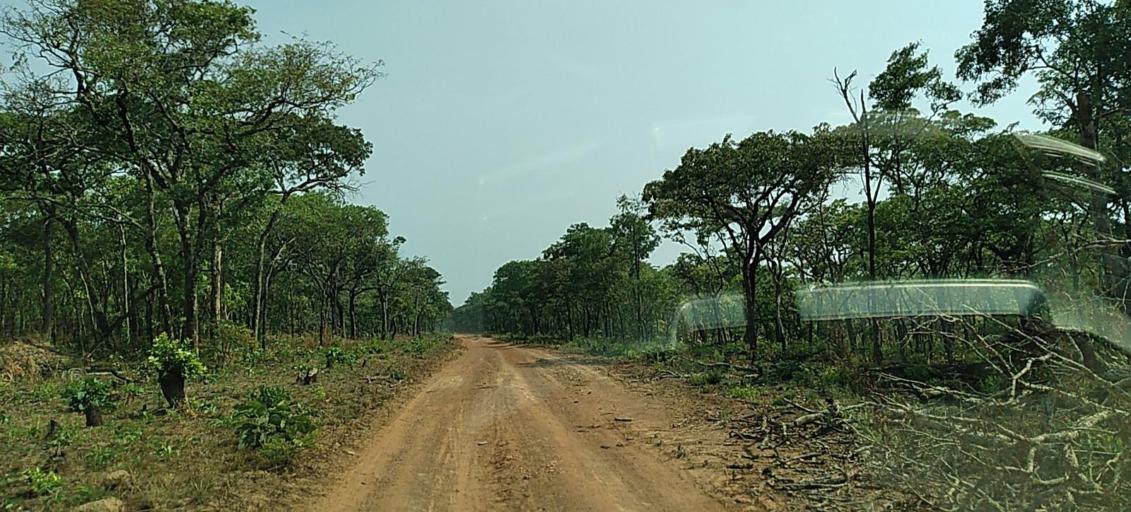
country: ZM
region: North-Western
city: Kansanshi
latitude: -12.0842
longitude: 26.8885
